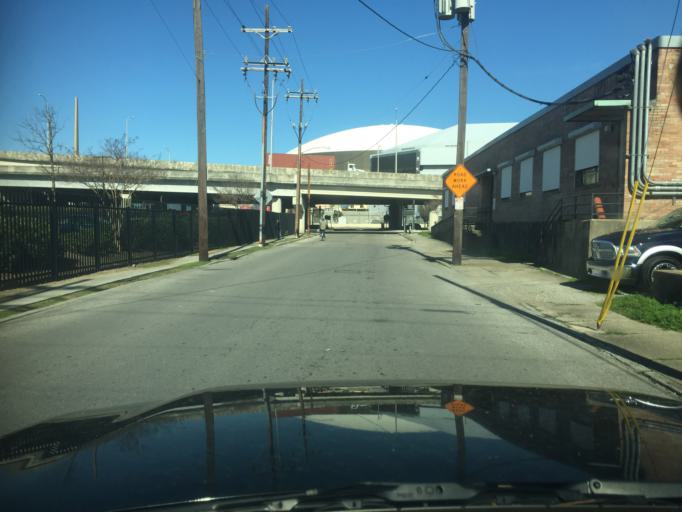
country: US
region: Louisiana
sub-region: Orleans Parish
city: New Orleans
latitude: 29.9473
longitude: -90.0841
